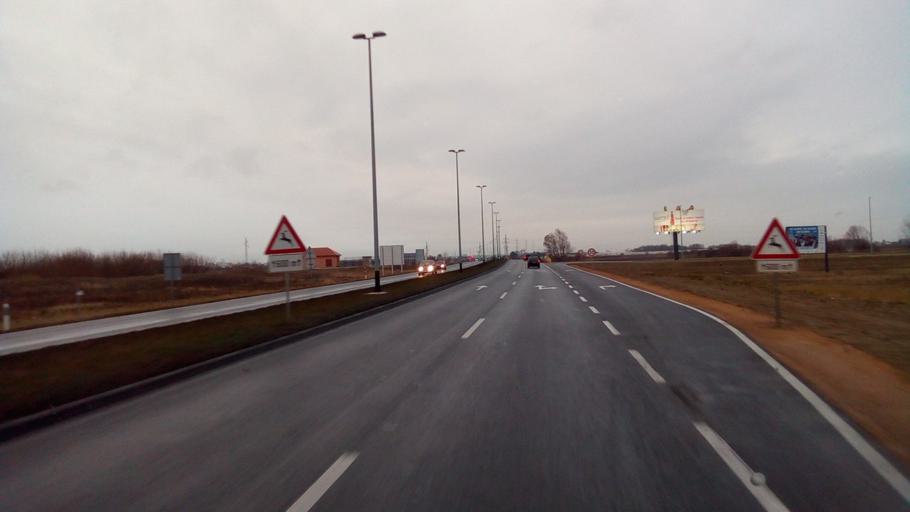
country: HR
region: Varazdinska
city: Varazdin
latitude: 46.2668
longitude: 16.3627
